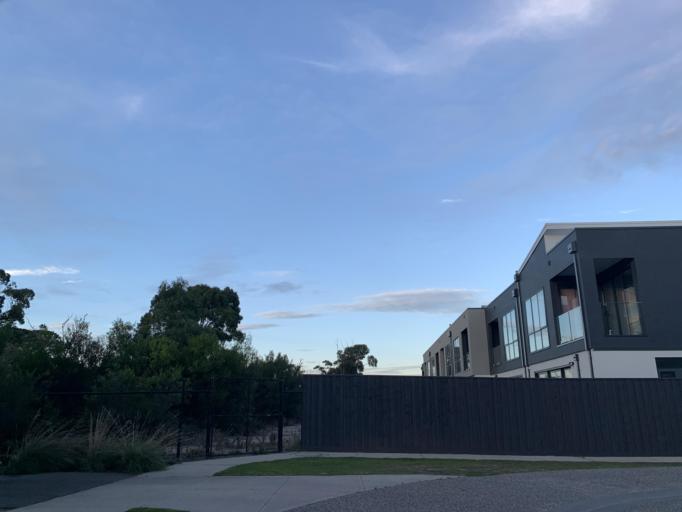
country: AU
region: Victoria
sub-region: Casey
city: Cranbourne North
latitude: -38.0719
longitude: 145.2780
